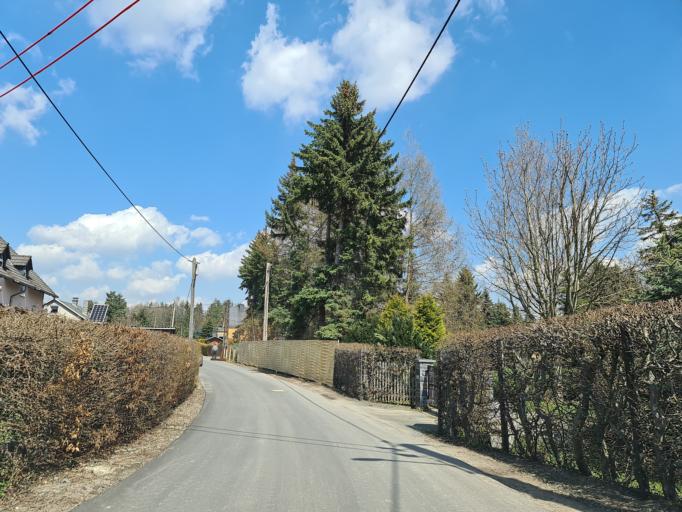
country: DE
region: Saxony
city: Oelsnitz
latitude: 50.7082
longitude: 12.7271
